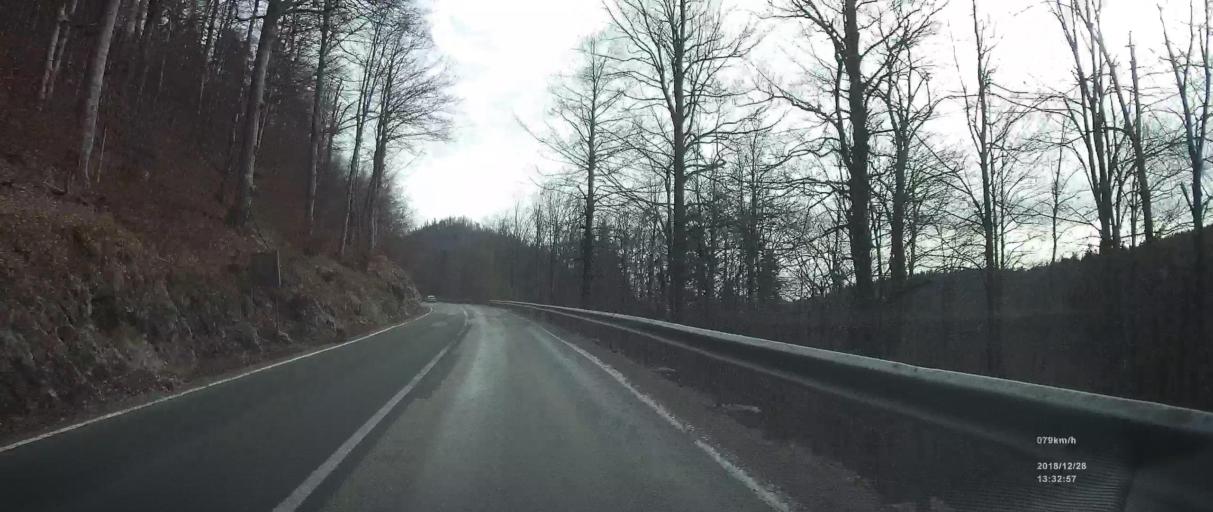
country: HR
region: Primorsko-Goranska
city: Hreljin
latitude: 45.3424
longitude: 14.6710
